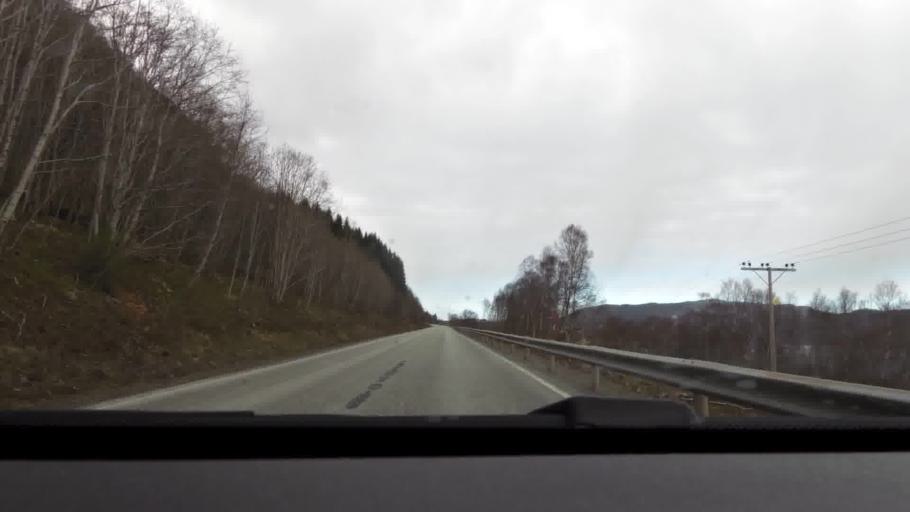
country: NO
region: More og Romsdal
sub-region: Eide
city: Eide
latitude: 62.9410
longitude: 7.4284
